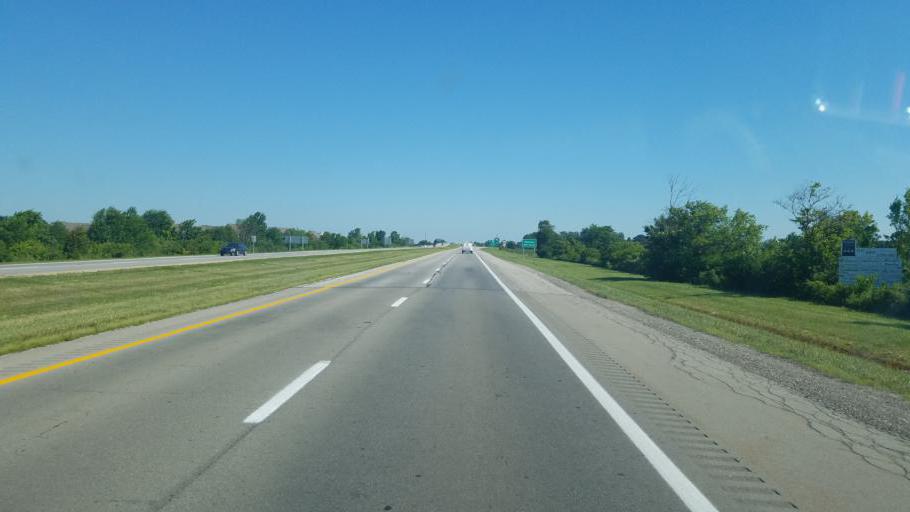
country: US
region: Ohio
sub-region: Marion County
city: Marion
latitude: 40.5874
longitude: -83.0794
